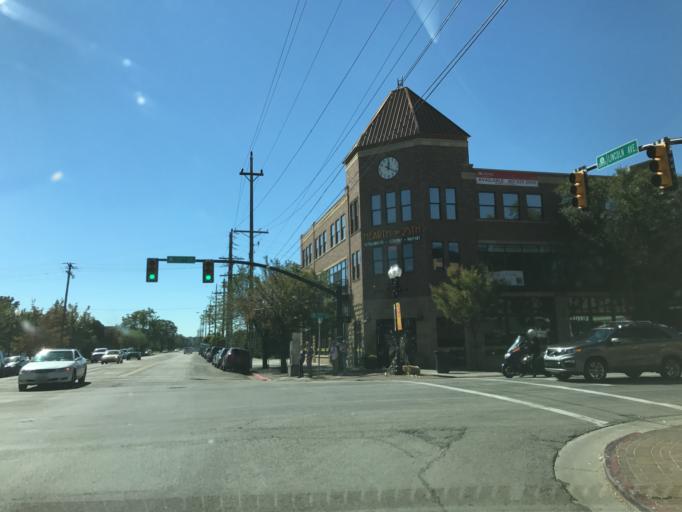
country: US
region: Utah
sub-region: Weber County
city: Ogden
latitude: 41.2209
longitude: -111.9761
